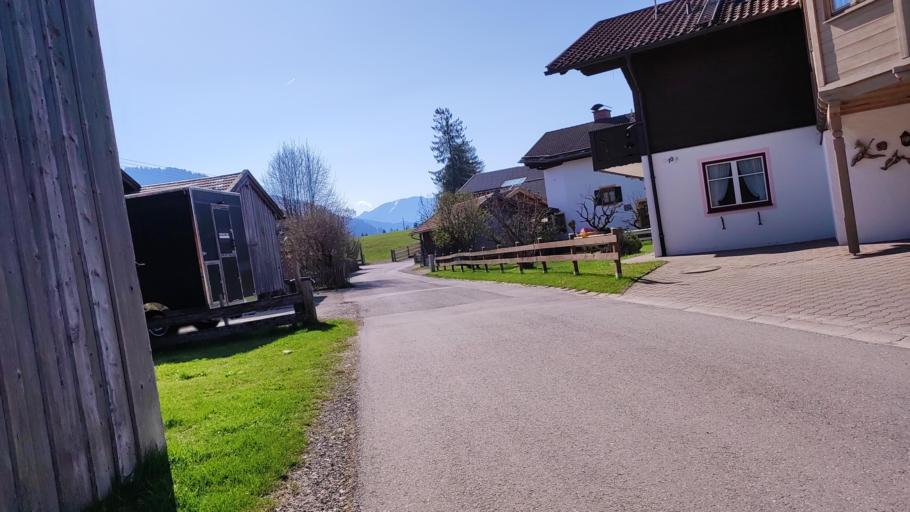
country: DE
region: Bavaria
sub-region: Upper Bavaria
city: Saulgrub
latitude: 47.6478
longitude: 11.0152
